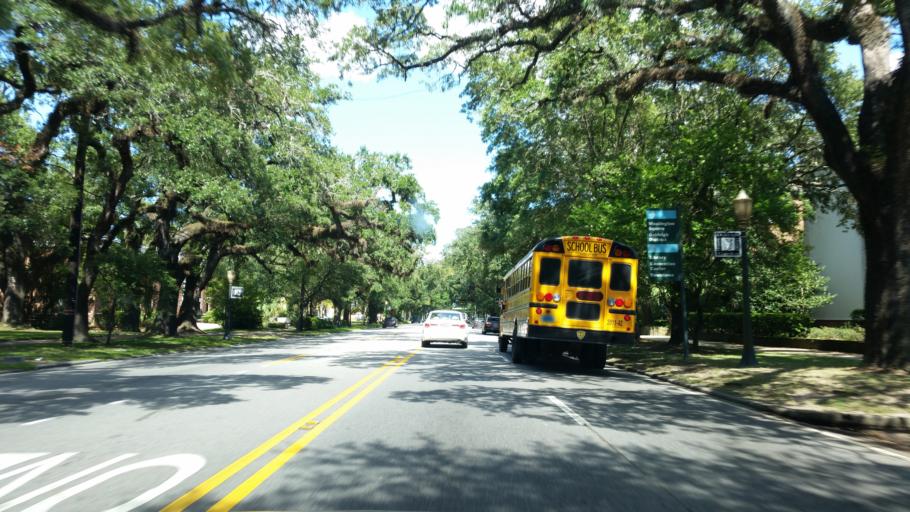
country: US
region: Alabama
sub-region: Mobile County
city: Mobile
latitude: 30.6846
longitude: -88.0590
